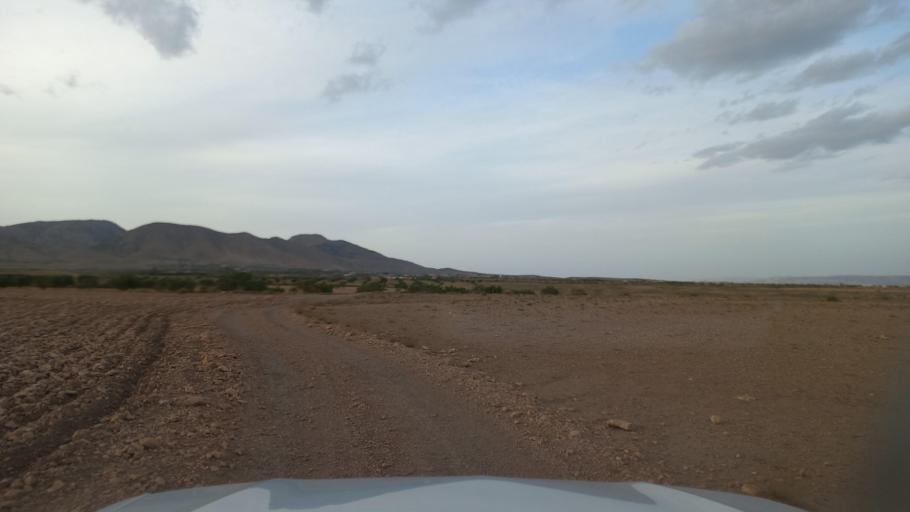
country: TN
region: Al Qasrayn
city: Sbiba
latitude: 35.4248
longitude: 9.0780
